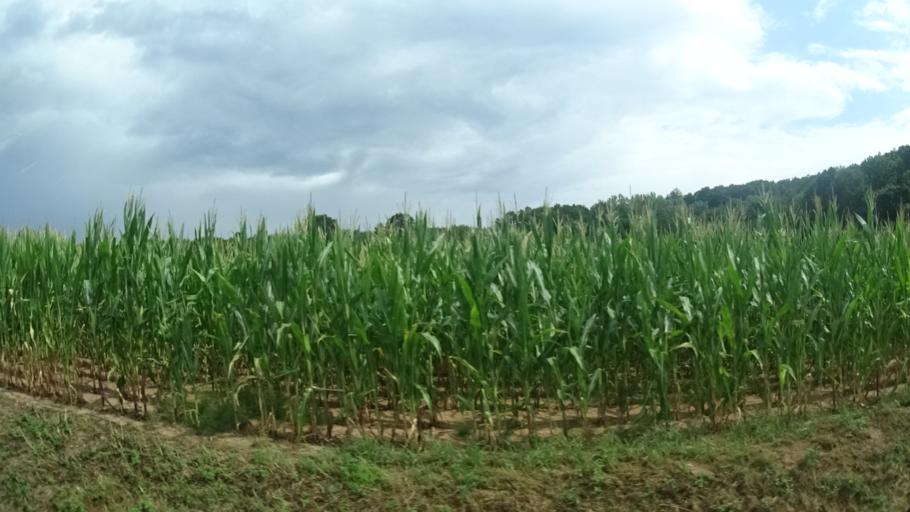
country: DE
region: Hesse
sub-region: Regierungsbezirk Kassel
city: Niederaula
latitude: 50.7997
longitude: 9.6330
